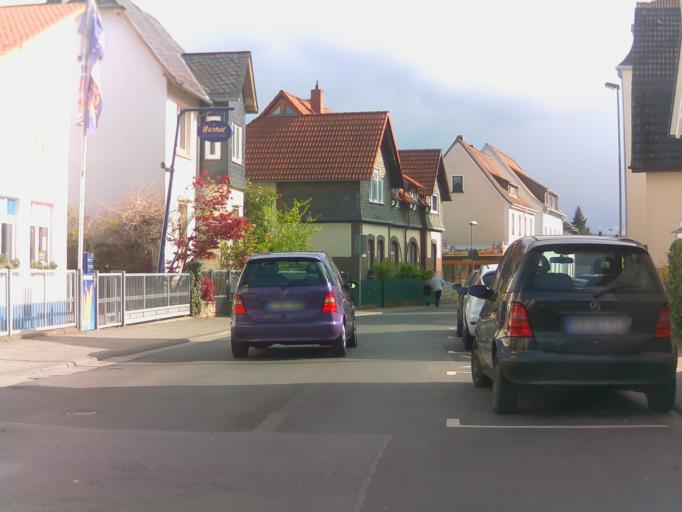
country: DE
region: Hesse
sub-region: Regierungsbezirk Darmstadt
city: Butzbach
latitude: 50.4311
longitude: 8.6643
